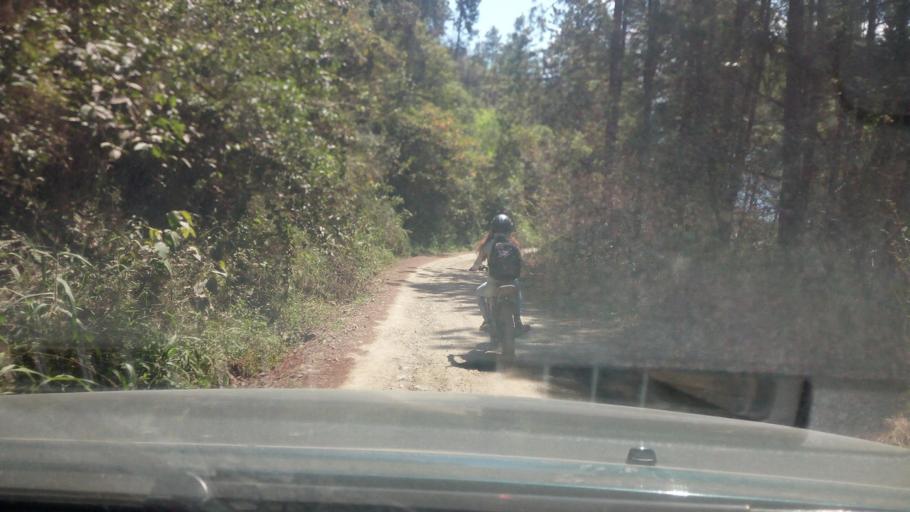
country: CO
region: Boyaca
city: Somondoco
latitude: 4.9922
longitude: -73.4171
